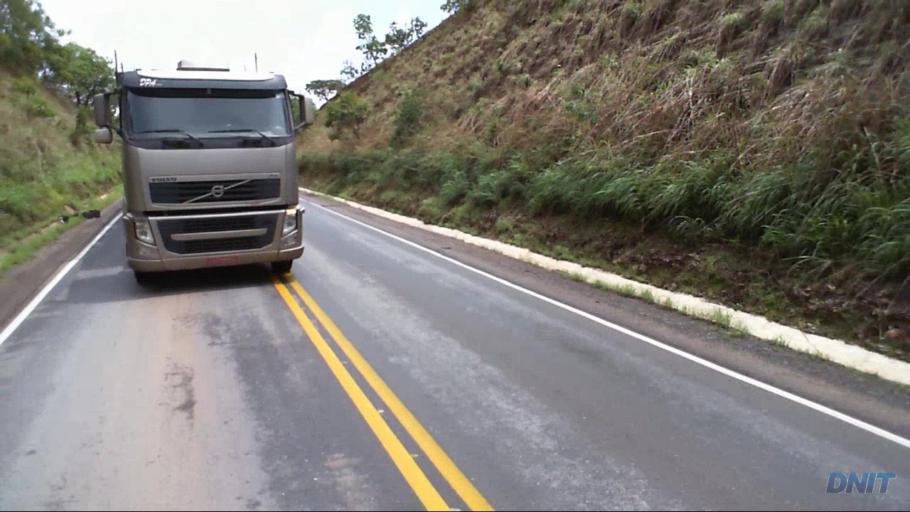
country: BR
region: Goias
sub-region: Padre Bernardo
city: Padre Bernardo
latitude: -15.4763
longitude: -48.2322
